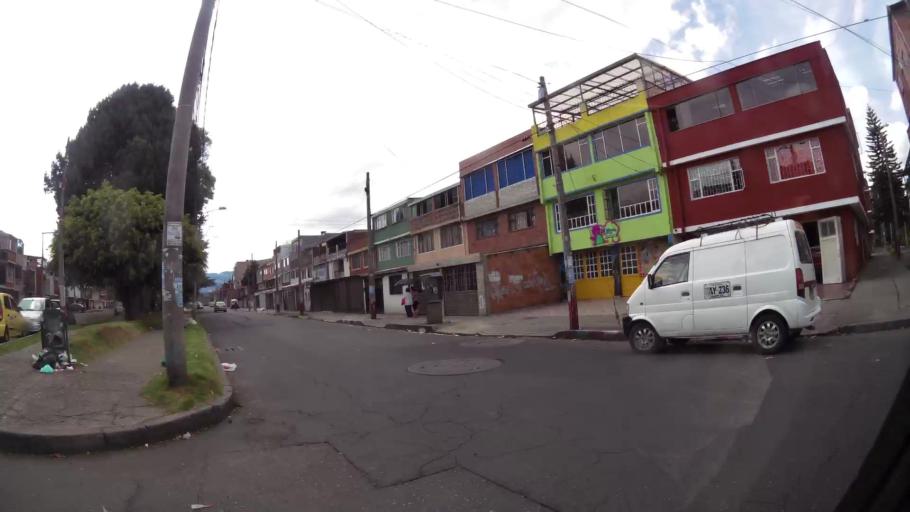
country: CO
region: Bogota D.C.
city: Bogota
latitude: 4.6970
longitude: -74.1124
